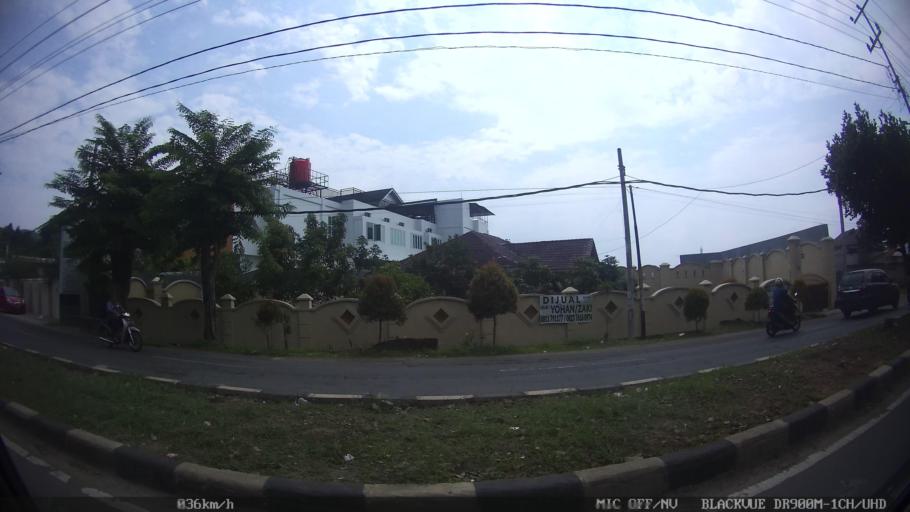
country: ID
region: Lampung
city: Bandarlampung
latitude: -5.4308
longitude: 105.2466
